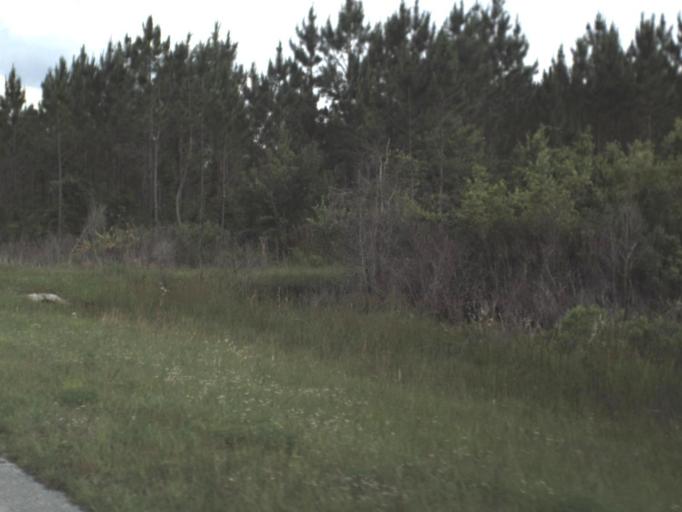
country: US
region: Florida
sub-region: Baker County
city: Macclenny
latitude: 30.5310
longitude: -82.3123
